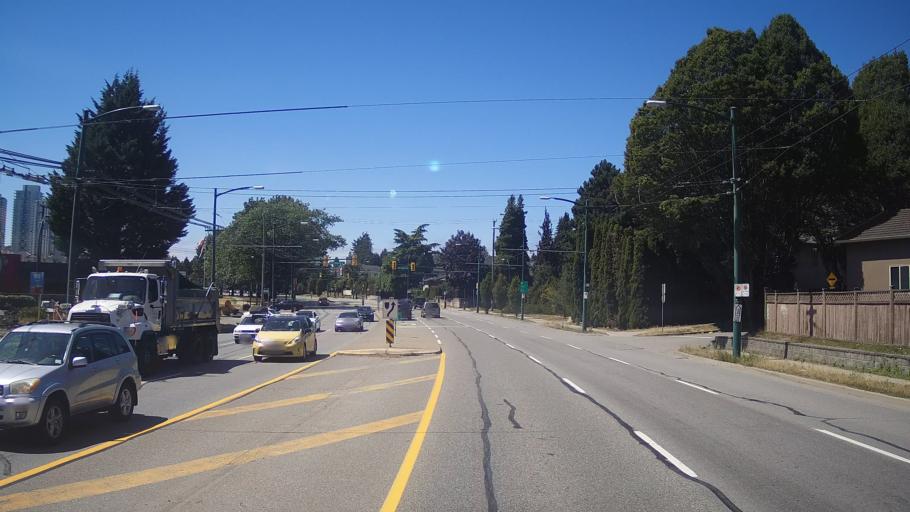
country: CA
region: British Columbia
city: Vancouver
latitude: 49.2120
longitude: -123.1050
